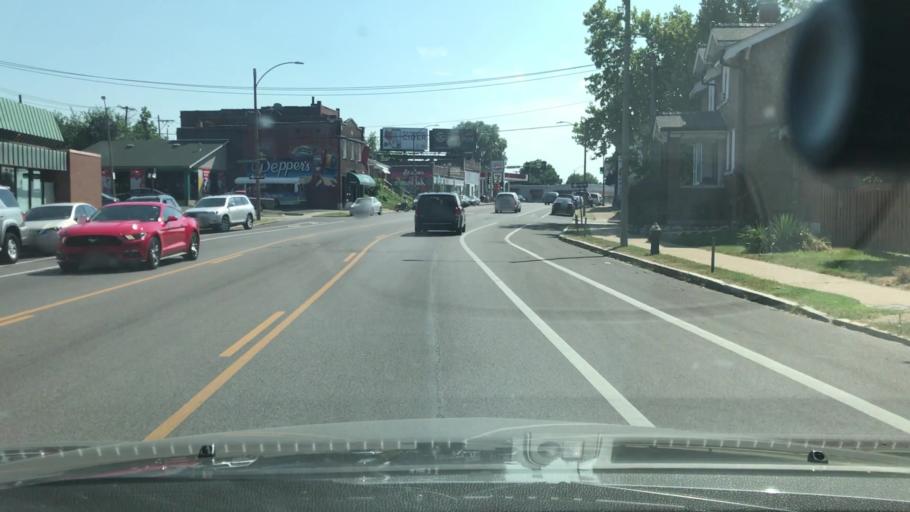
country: US
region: Missouri
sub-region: Saint Louis County
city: Lemay
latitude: 38.5786
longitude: -90.2707
